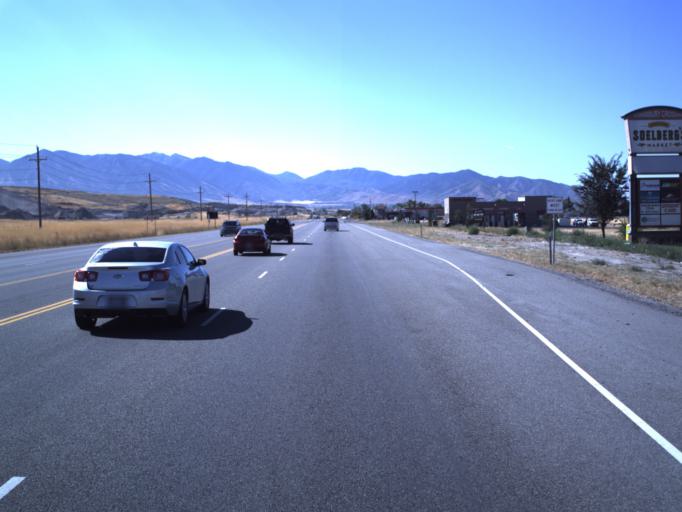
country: US
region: Utah
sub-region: Tooele County
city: Stansbury park
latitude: 40.6520
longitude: -112.2891
